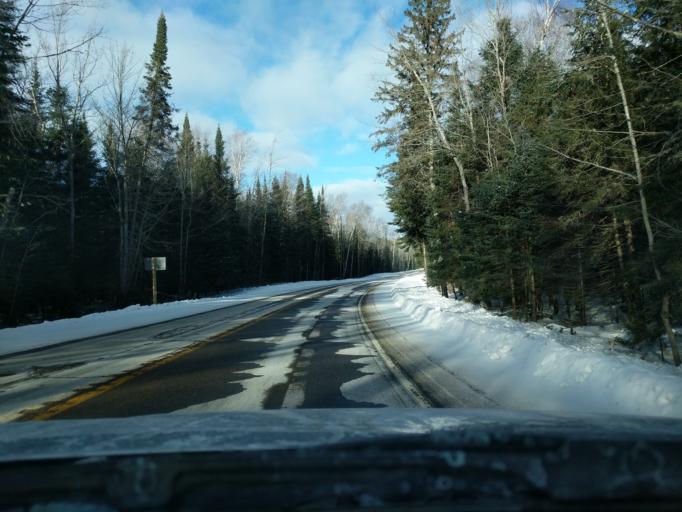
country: US
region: Wisconsin
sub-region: Vilas County
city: Eagle River
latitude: 45.7663
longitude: -89.0682
